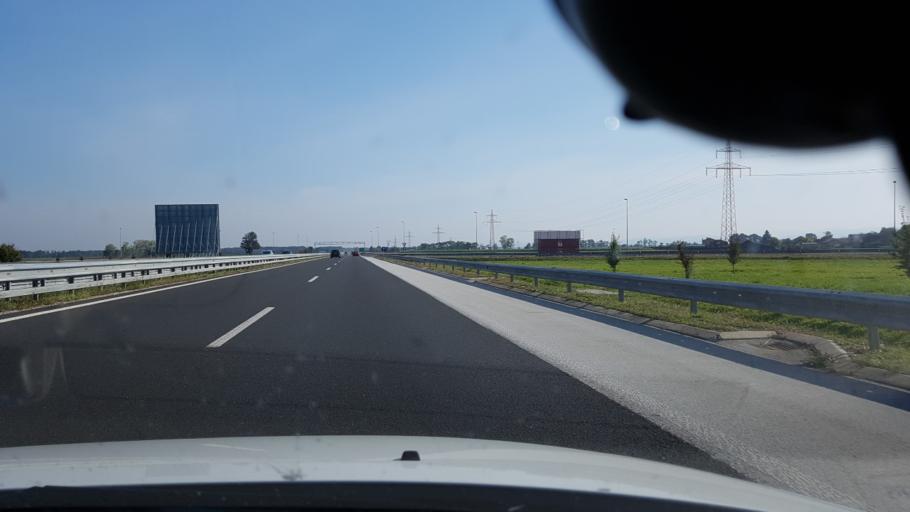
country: SI
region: Hoce-Slivnica
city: Hotinja Vas
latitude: 46.4739
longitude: 15.6762
